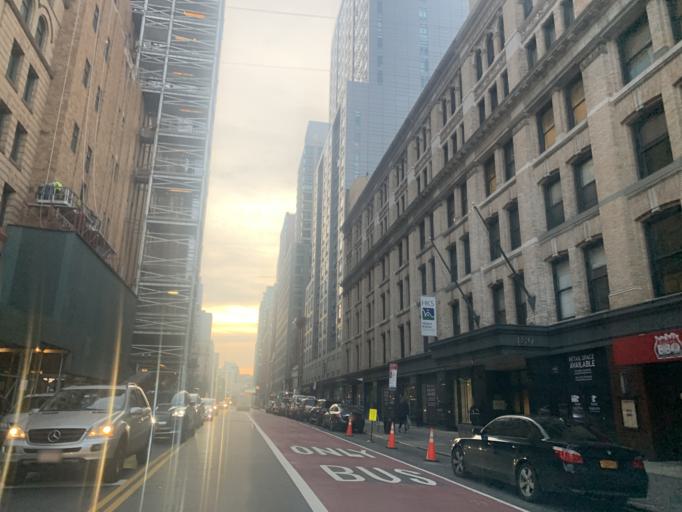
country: US
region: New York
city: New York City
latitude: 40.6902
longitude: -73.9873
